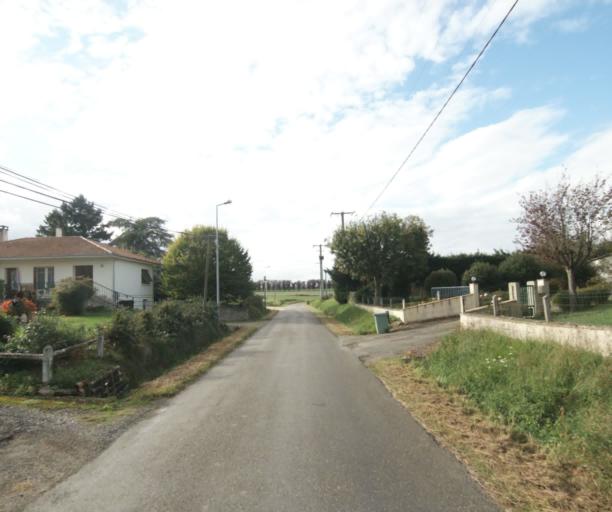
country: FR
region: Midi-Pyrenees
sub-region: Departement du Gers
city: Eauze
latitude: 43.8683
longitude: 0.0941
